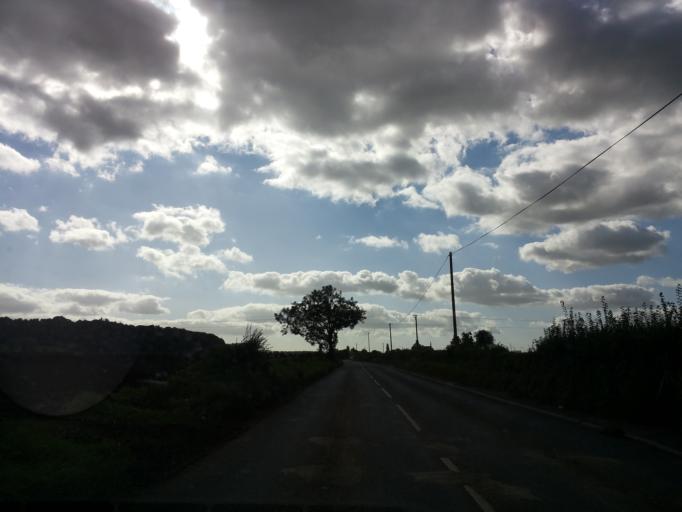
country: GB
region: England
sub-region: Bath and North East Somerset
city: Saltford
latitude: 51.3815
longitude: -2.4626
